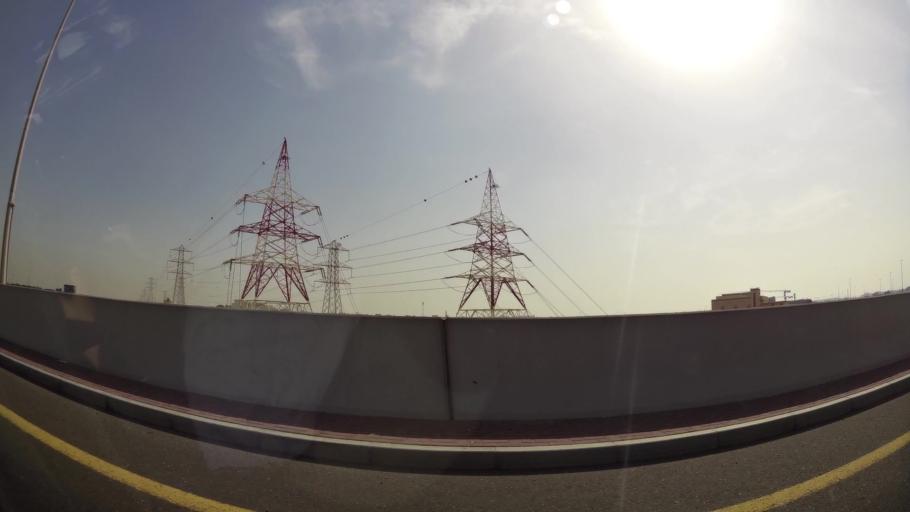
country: AE
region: Ash Shariqah
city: Sharjah
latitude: 25.2360
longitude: 55.4055
